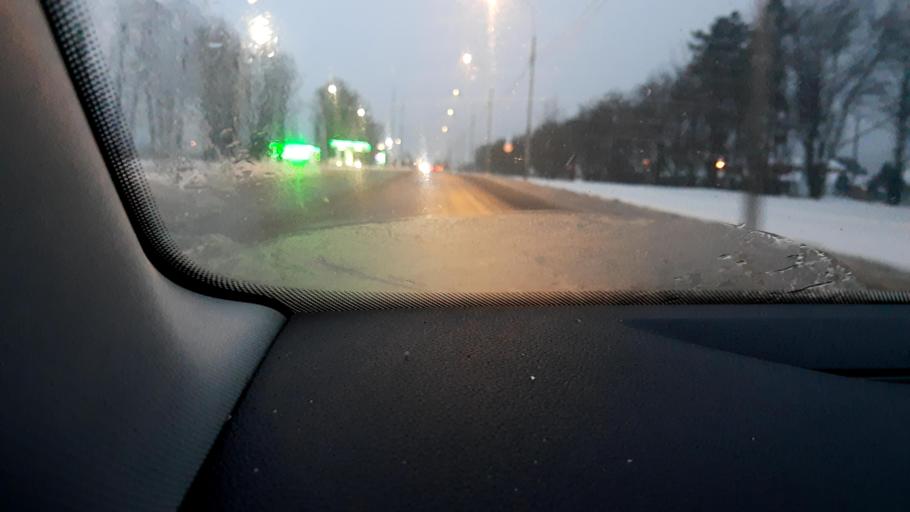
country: RU
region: Moskovskaya
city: Troitsk
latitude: 55.3303
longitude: 37.1660
